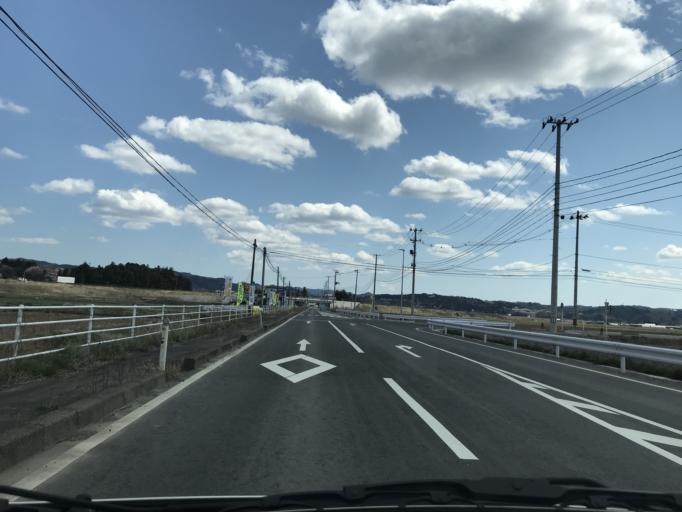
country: JP
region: Miyagi
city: Wakuya
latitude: 38.6710
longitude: 141.2619
